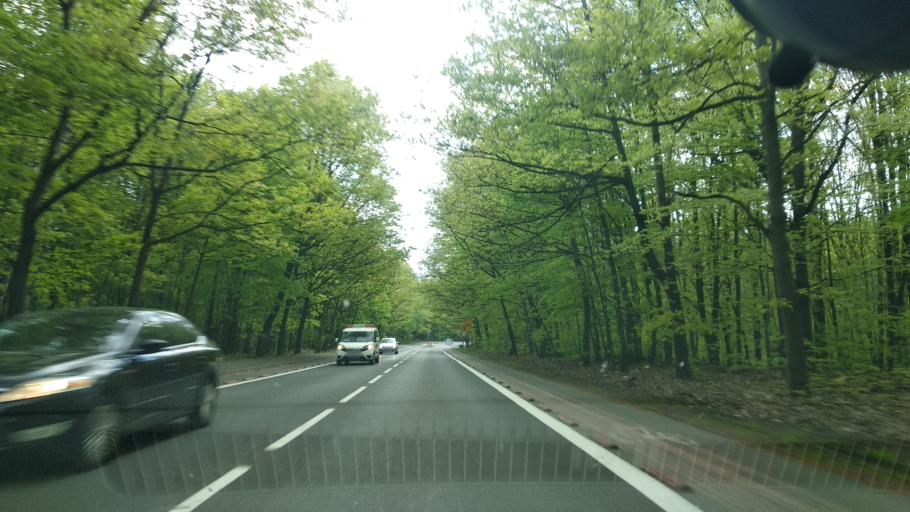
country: PL
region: Silesian Voivodeship
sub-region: Ruda Slaska
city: Ruda Slaska
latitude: 50.2355
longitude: 18.9119
